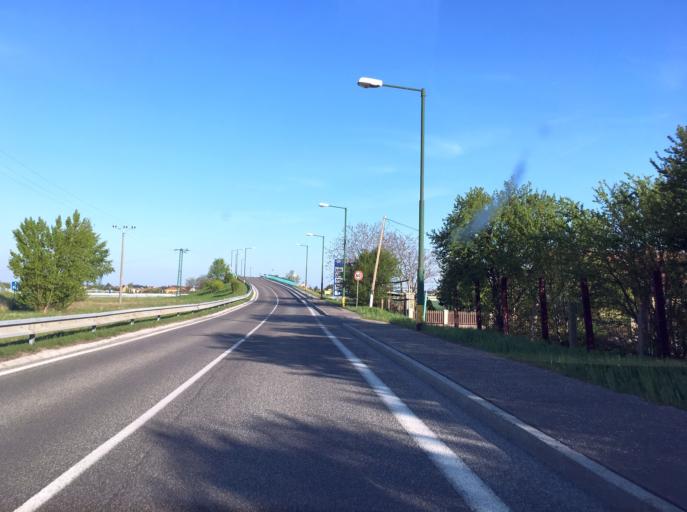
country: AT
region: Burgenland
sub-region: Politischer Bezirk Neusiedl am See
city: Kittsee
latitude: 48.0706
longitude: 17.0989
